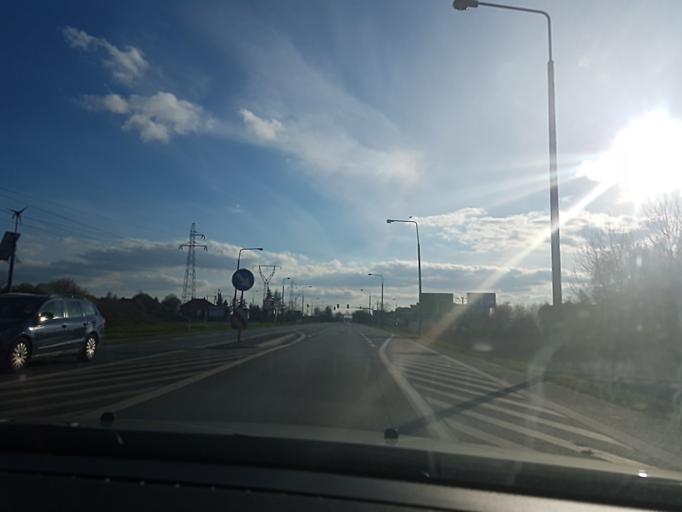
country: PL
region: Lodz Voivodeship
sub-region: Powiat kutnowski
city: Kutno
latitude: 52.2158
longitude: 19.3829
